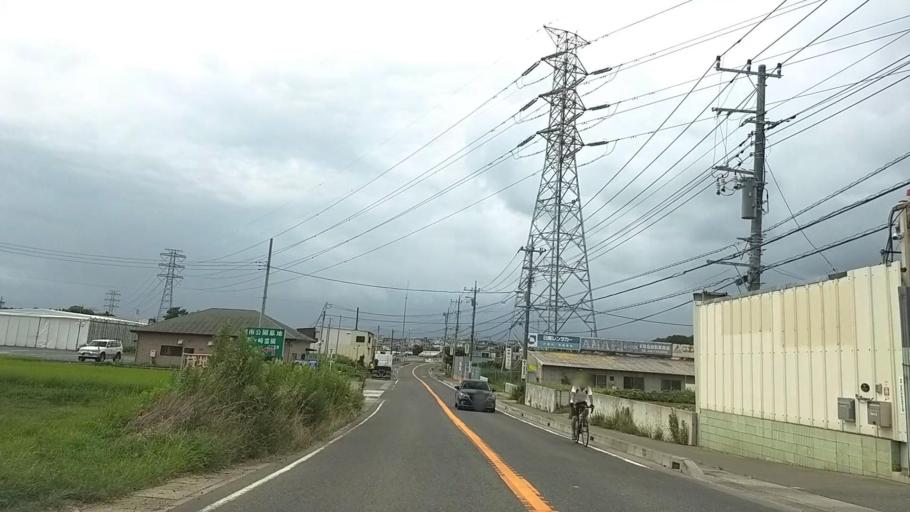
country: JP
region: Kanagawa
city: Chigasaki
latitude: 35.3676
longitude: 139.4031
